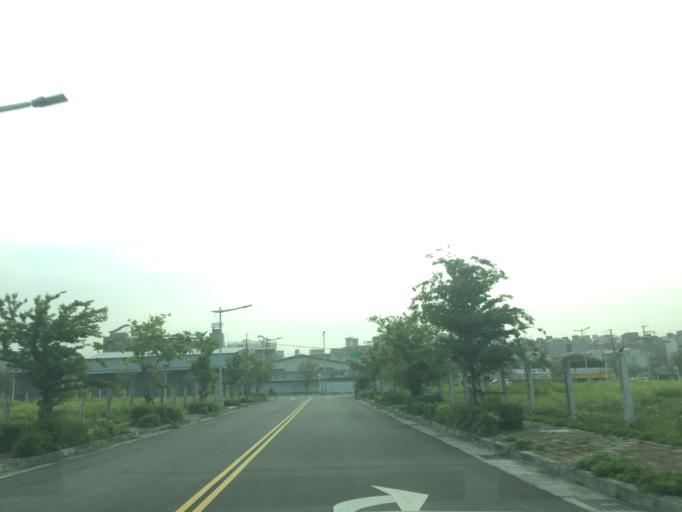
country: TW
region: Taiwan
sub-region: Taichung City
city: Taichung
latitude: 24.1966
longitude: 120.6924
